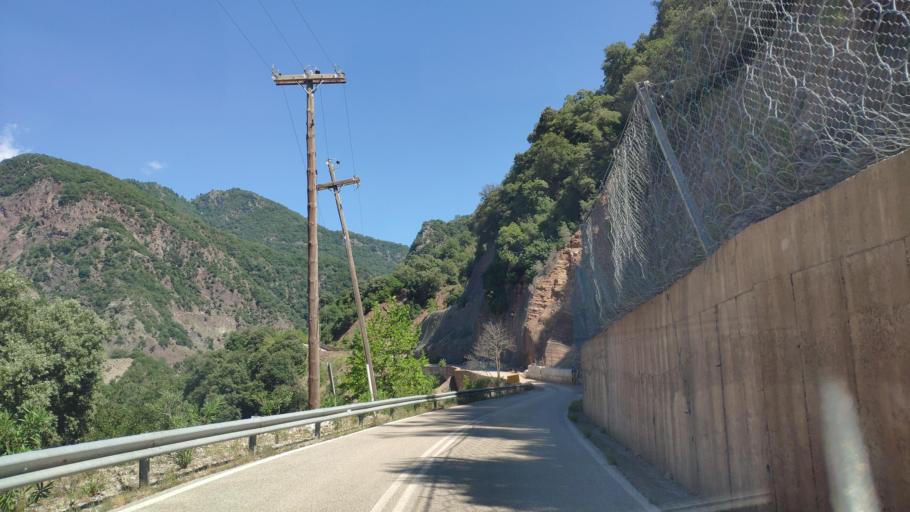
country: GR
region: Central Greece
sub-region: Nomos Evrytanias
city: Kerasochori
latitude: 39.0413
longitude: 21.5962
